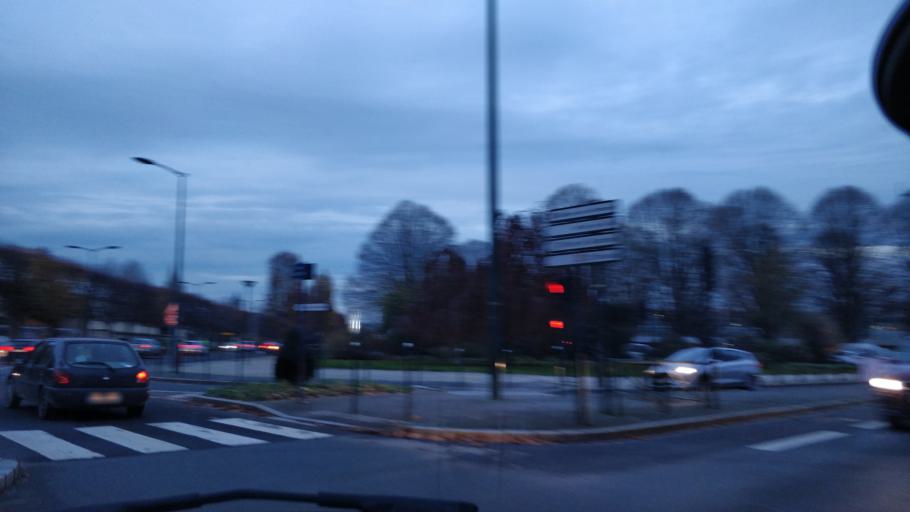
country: FR
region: Lower Normandy
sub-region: Departement du Calvados
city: Caen
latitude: 49.1751
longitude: -0.3708
